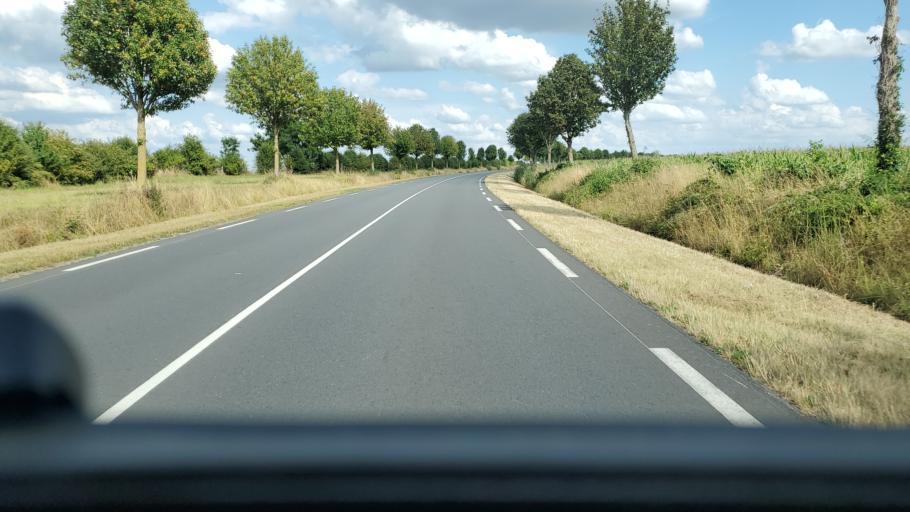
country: FR
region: Ile-de-France
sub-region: Departement de Seine-et-Marne
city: Nanteuil-les-Meaux
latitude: 48.9142
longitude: 2.9099
